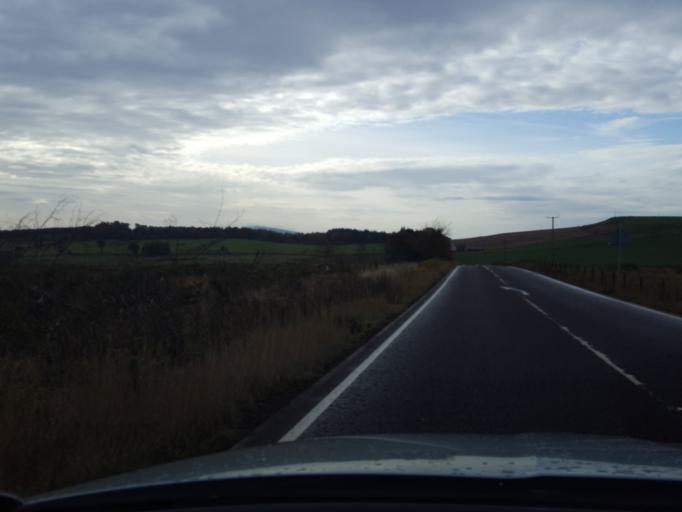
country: GB
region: Scotland
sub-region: South Lanarkshire
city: Carnwath
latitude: 55.7259
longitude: -3.5770
